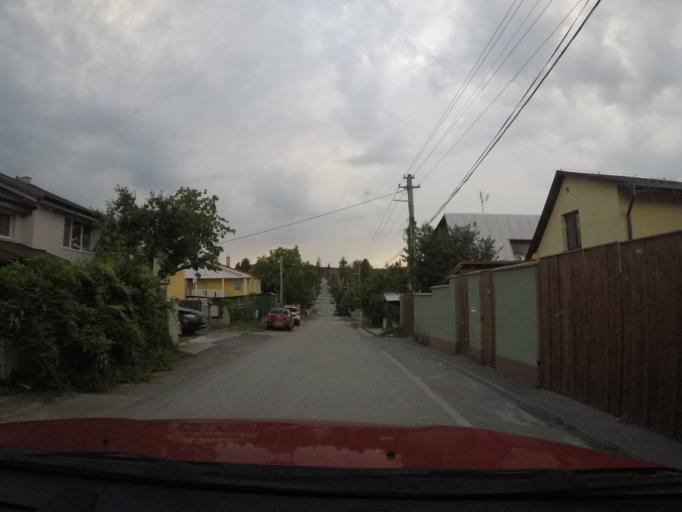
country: SK
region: Kosicky
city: Kosice
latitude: 48.6900
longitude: 21.2134
